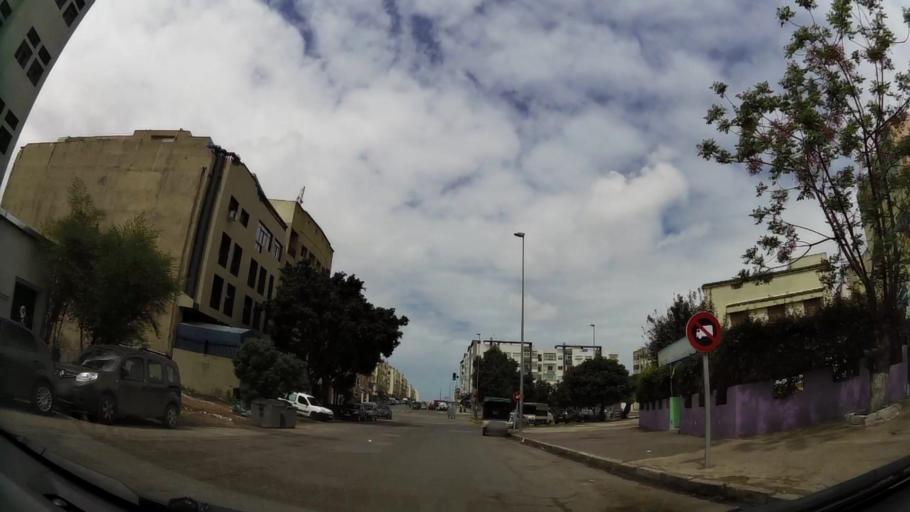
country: MA
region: Grand Casablanca
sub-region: Casablanca
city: Casablanca
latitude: 33.5376
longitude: -7.6023
